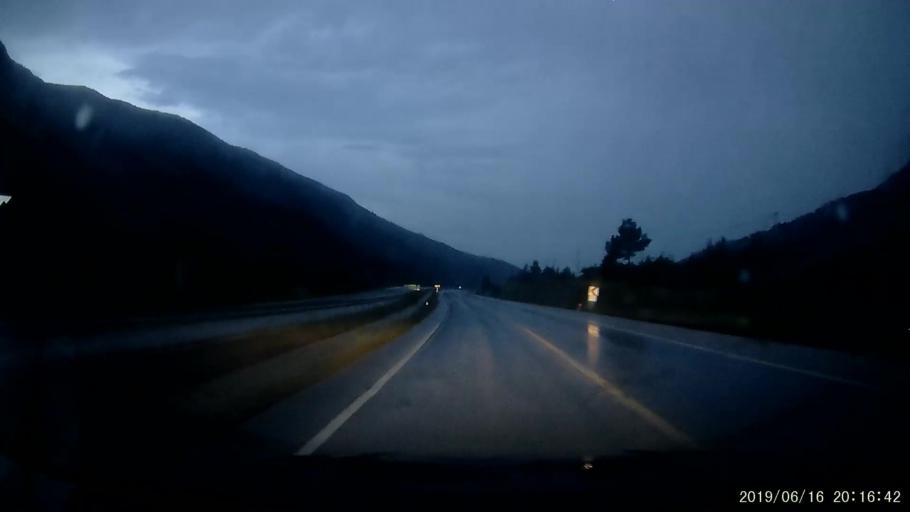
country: TR
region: Tokat
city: Resadiye
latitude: 40.3603
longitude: 37.4363
